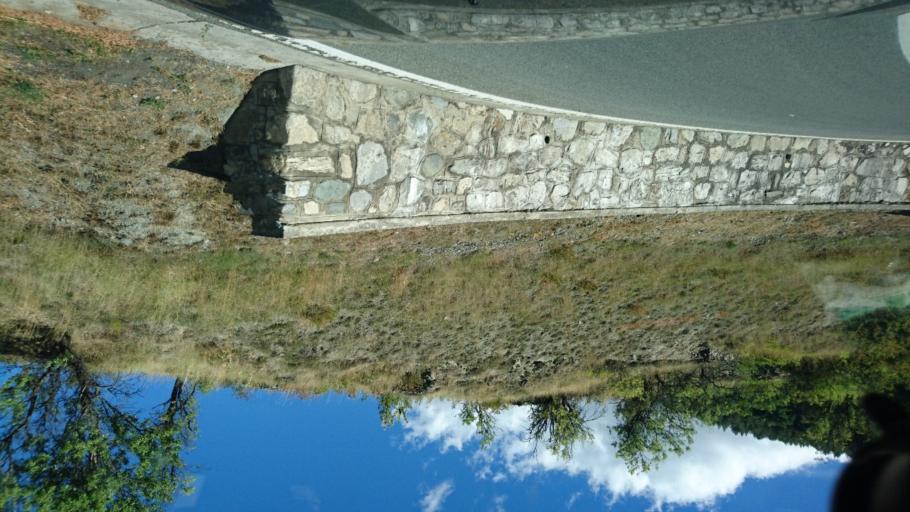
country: IT
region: Aosta Valley
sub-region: Valle d'Aosta
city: Villeneuve
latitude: 45.7099
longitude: 7.2096
